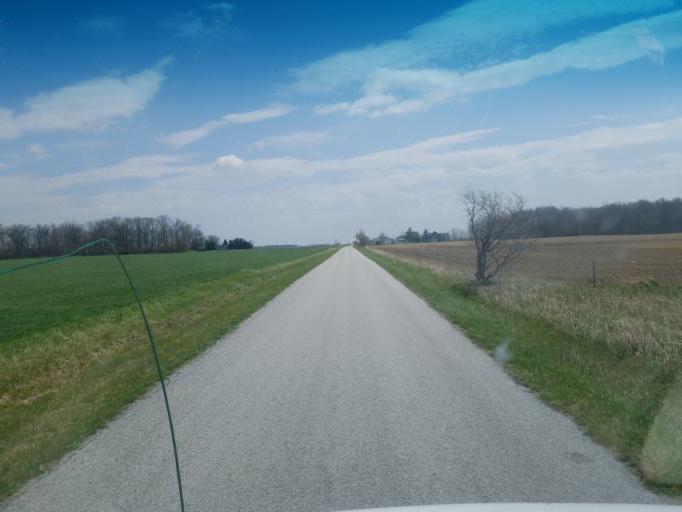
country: US
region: Ohio
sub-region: Hardin County
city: Forest
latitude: 40.7743
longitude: -83.4718
